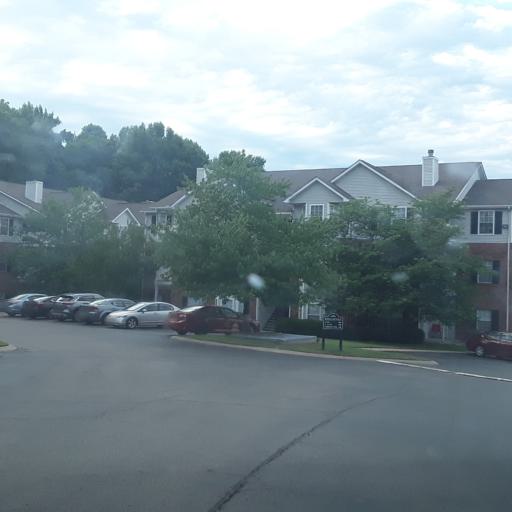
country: US
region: Tennessee
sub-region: Wilson County
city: Green Hill
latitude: 36.1661
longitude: -86.6003
